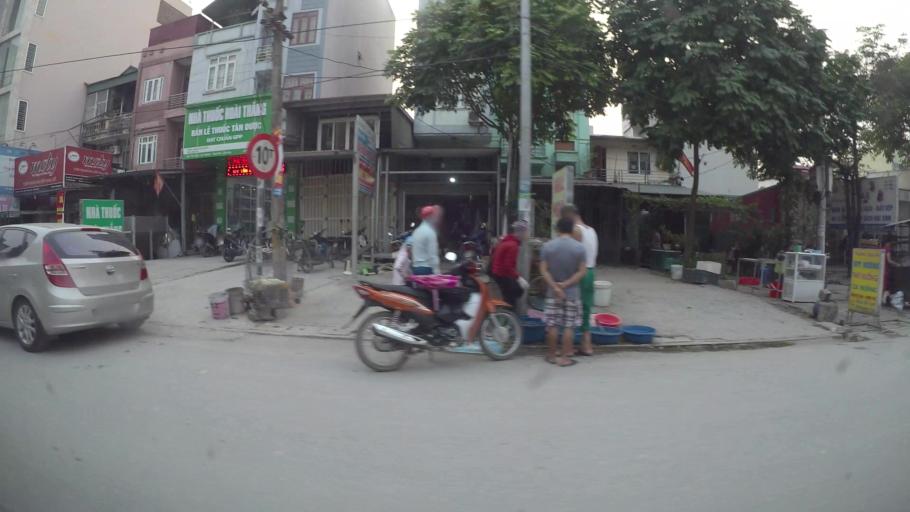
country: VN
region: Ha Noi
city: Cau Dien
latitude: 21.0075
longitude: 105.7204
